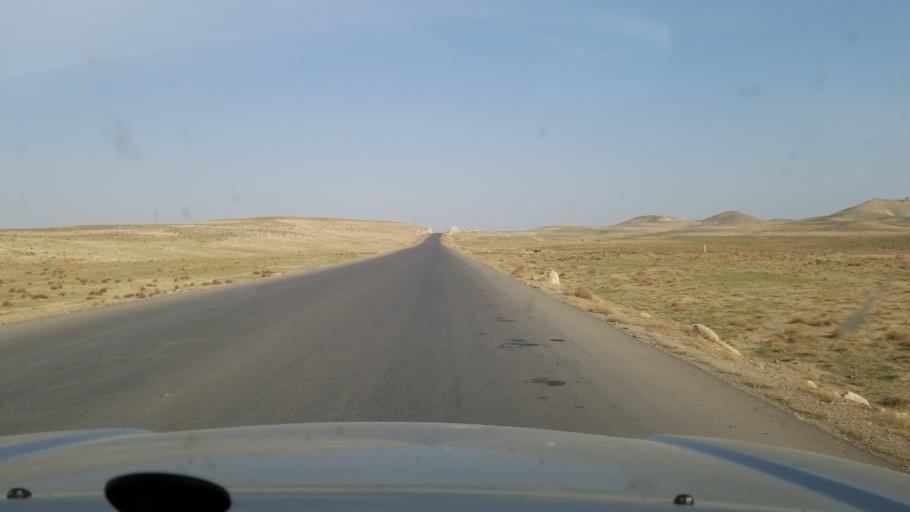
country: AF
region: Jowzjan
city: Khamyab
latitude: 37.6212
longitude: 65.7009
